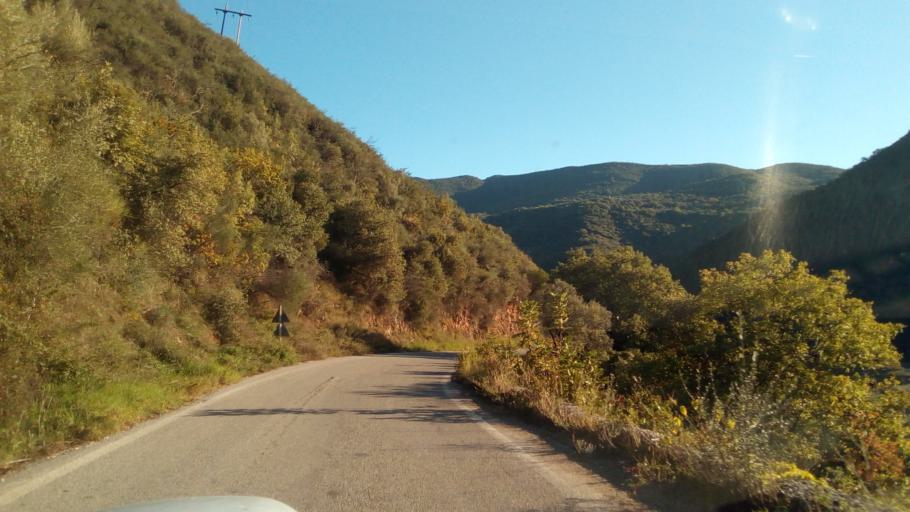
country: GR
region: West Greece
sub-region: Nomos Aitolias kai Akarnanias
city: Nafpaktos
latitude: 38.4382
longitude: 21.8792
